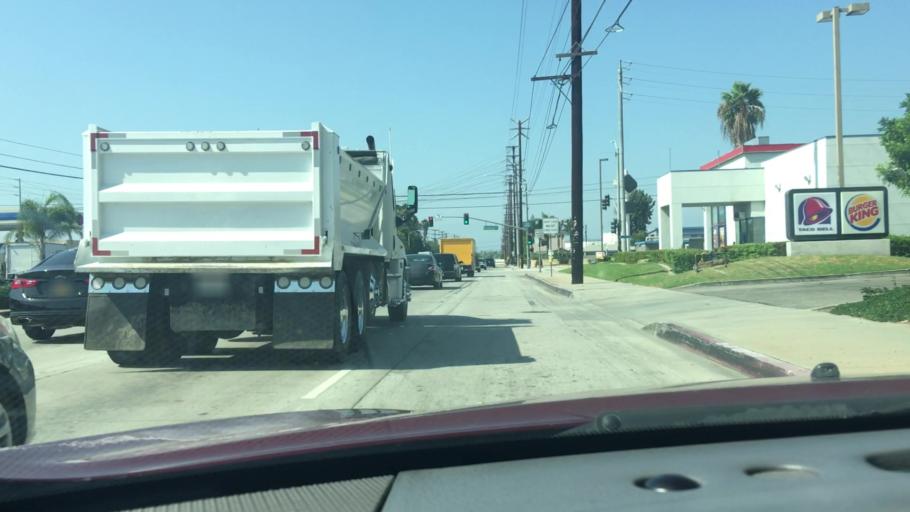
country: US
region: California
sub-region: Los Angeles County
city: Norwalk
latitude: 33.9016
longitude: -118.0465
